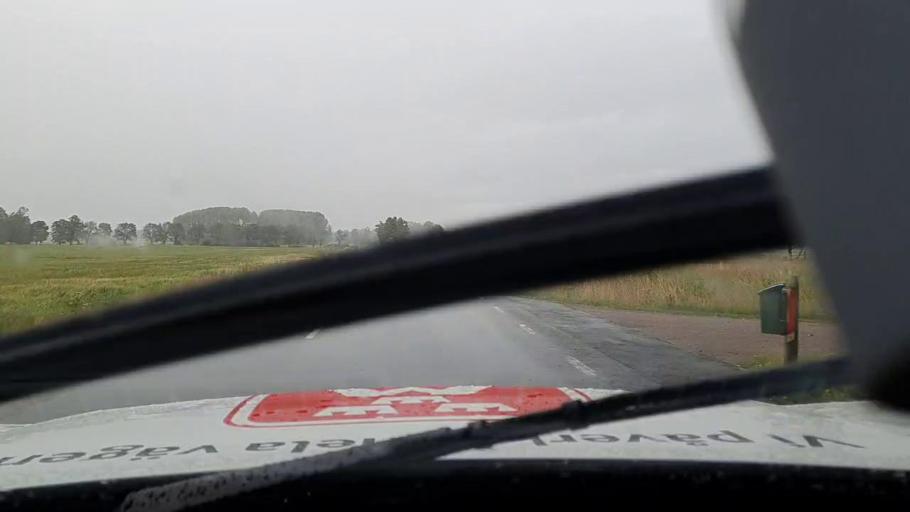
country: SE
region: Vaestra Goetaland
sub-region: Toreboda Kommun
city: Toereboda
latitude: 58.6693
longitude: 14.1325
